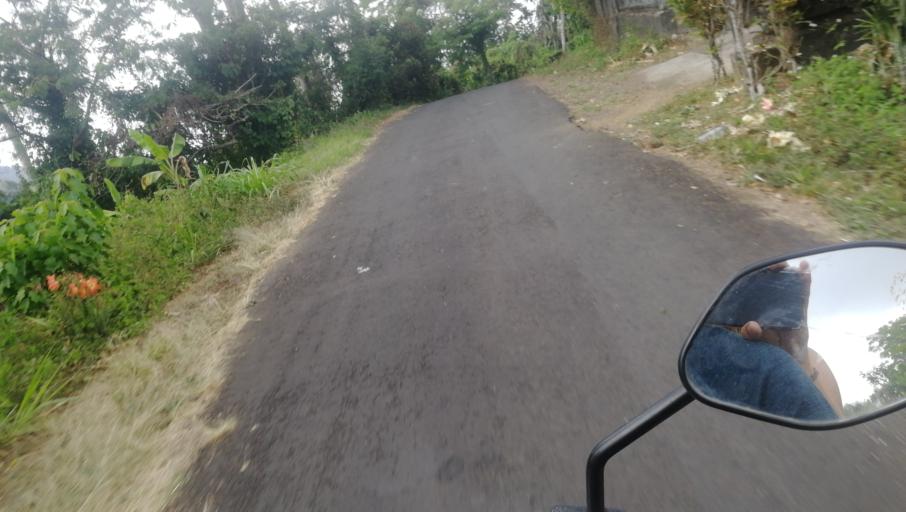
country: ID
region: Bali
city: Banjar Ambengan
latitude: -8.2140
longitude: 115.1095
